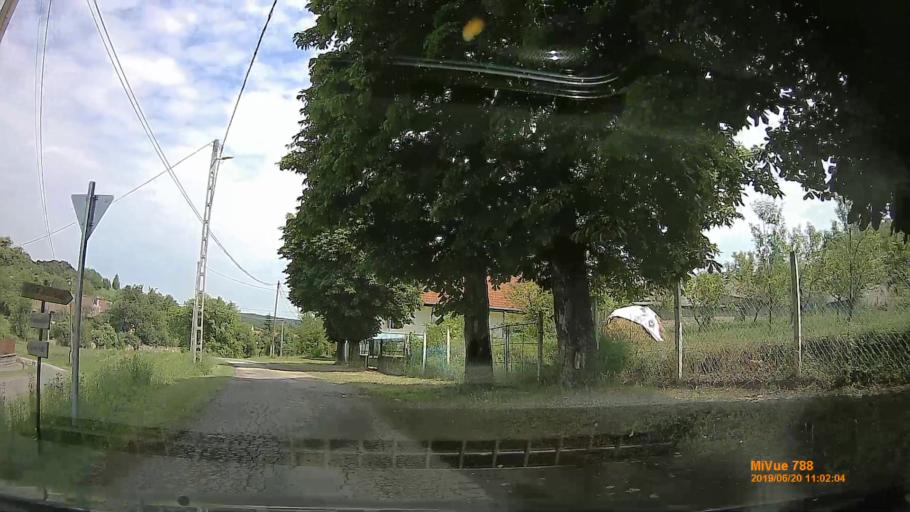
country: HU
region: Baranya
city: Mecseknadasd
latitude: 46.1776
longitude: 18.5116
